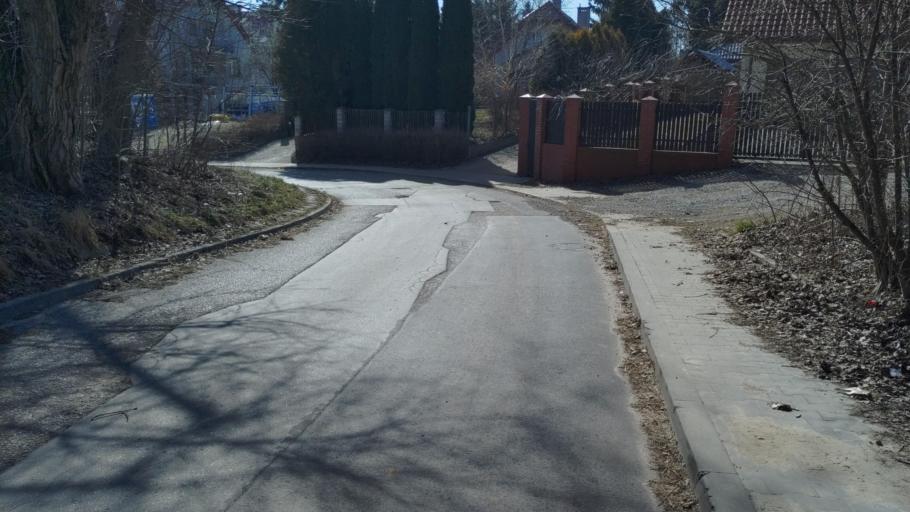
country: PL
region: Lesser Poland Voivodeship
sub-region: Powiat krakowski
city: Rzaska
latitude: 50.0905
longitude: 19.8747
